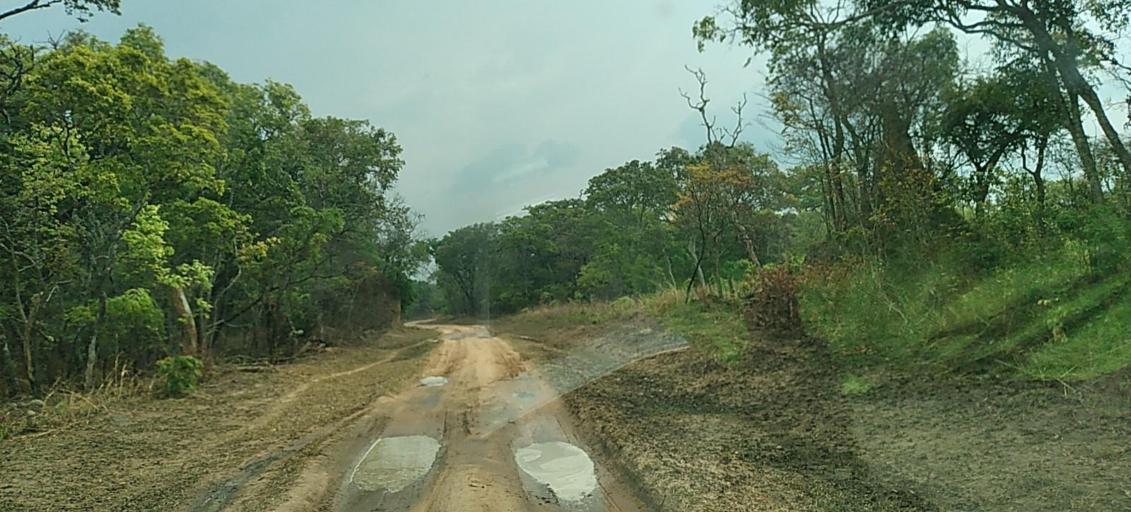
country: ZM
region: North-Western
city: Mwinilunga
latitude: -11.4676
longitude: 24.4684
